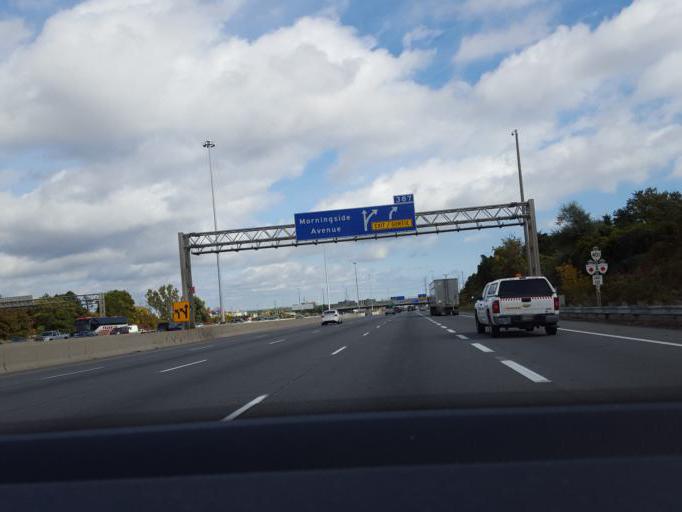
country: CA
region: Ontario
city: Scarborough
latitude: 43.7945
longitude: -79.2083
